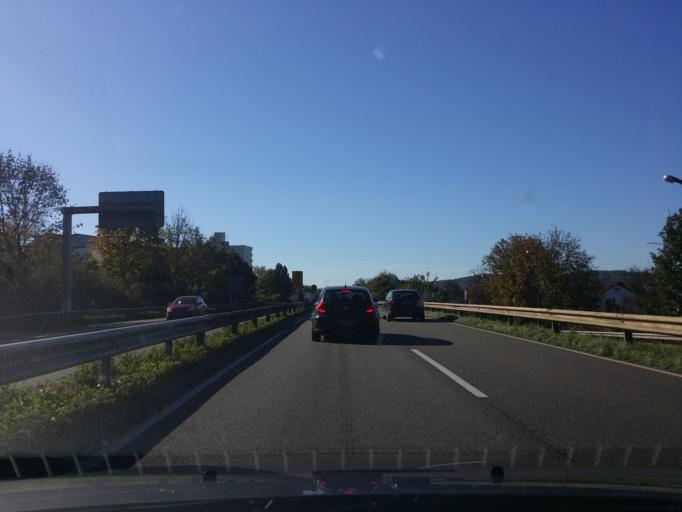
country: DE
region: Baden-Wuerttemberg
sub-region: Tuebingen Region
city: Tuebingen
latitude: 48.5132
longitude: 9.0768
